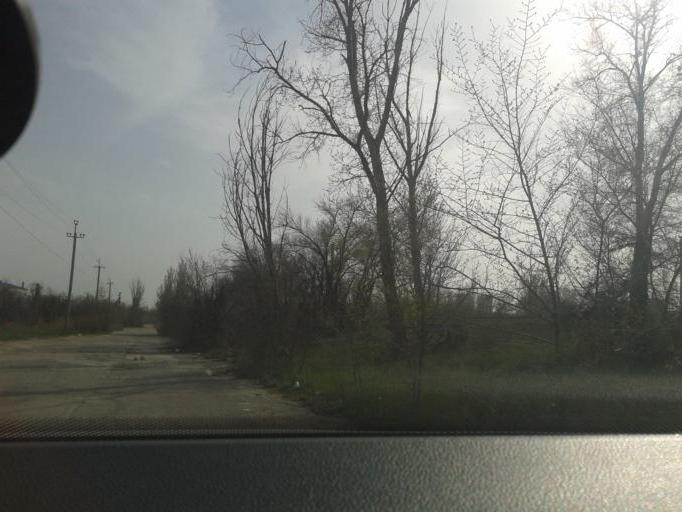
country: RU
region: Volgograd
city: Volgograd
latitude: 48.6354
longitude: 44.4390
